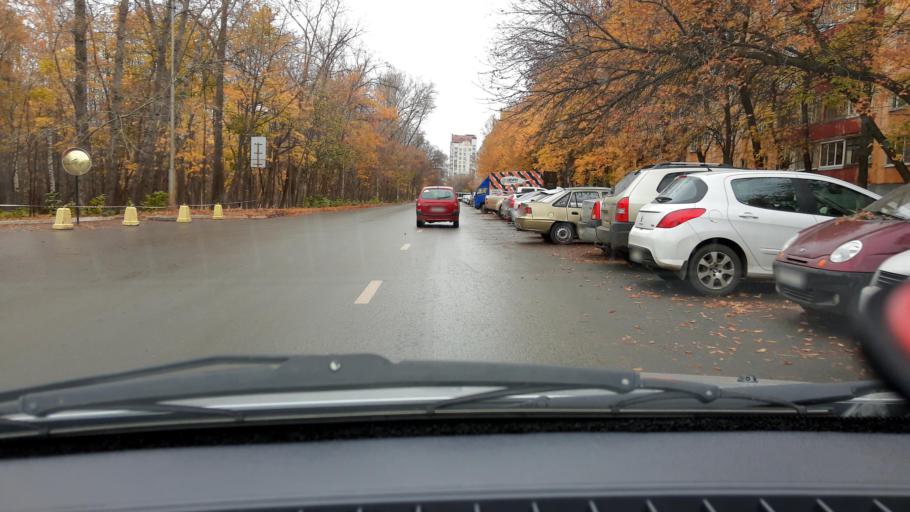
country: RU
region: Bashkortostan
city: Ufa
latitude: 54.7407
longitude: 56.0188
